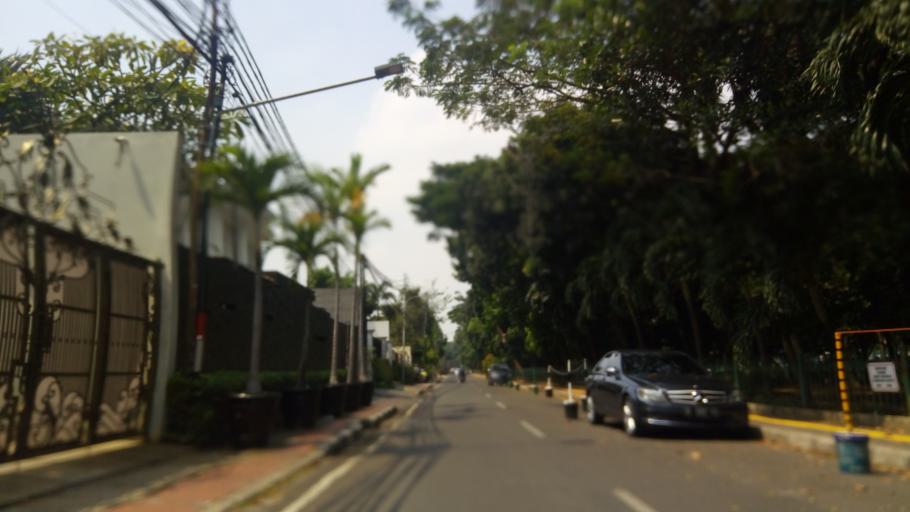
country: ID
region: Jakarta Raya
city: Jakarta
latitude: -6.1986
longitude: 106.8240
